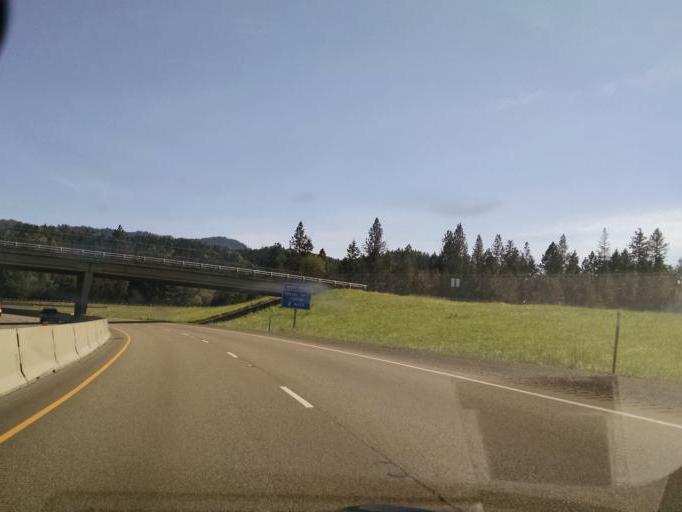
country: US
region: Oregon
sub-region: Douglas County
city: Riddle
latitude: 42.9503
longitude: -123.3305
